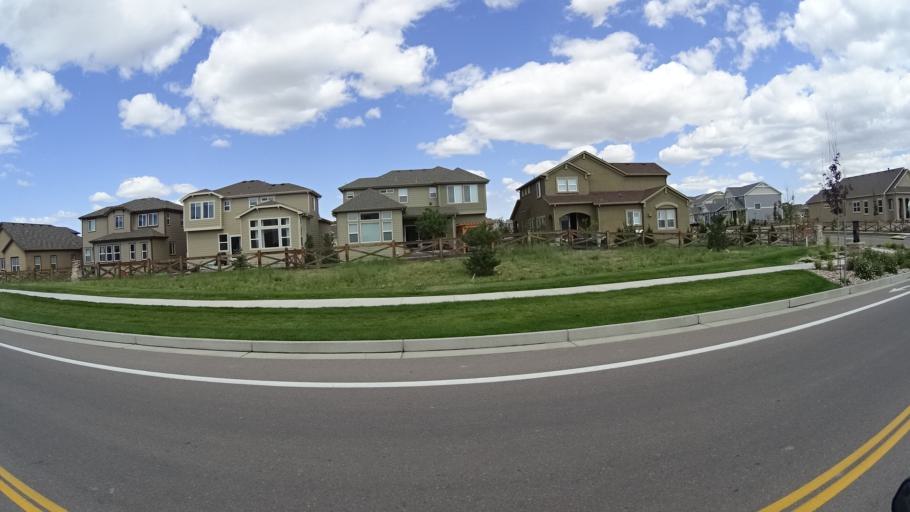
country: US
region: Colorado
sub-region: El Paso County
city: Cimarron Hills
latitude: 38.9330
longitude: -104.6593
